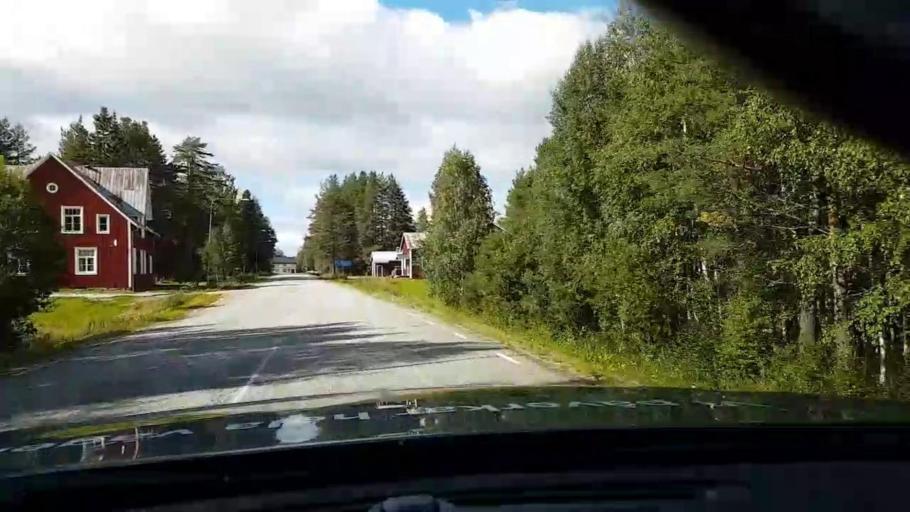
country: SE
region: Vaesterbotten
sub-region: Asele Kommun
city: Asele
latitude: 63.9364
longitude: 17.2867
